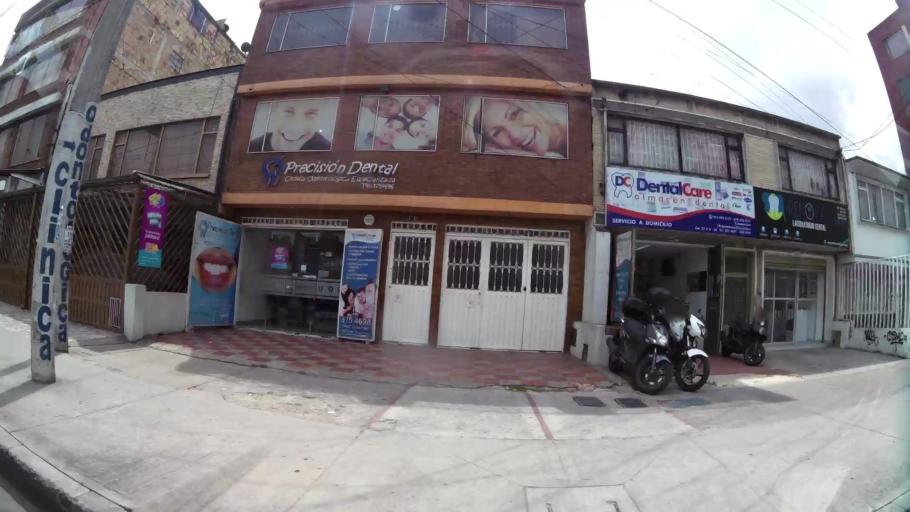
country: CO
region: Bogota D.C.
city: Bogota
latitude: 4.6001
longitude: -74.0988
